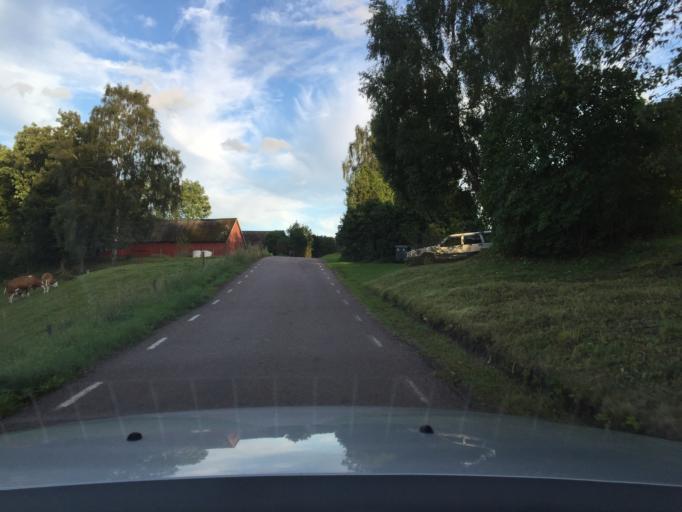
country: SE
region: Skane
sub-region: Hassleholms Kommun
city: Sosdala
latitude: 56.0304
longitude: 13.7511
